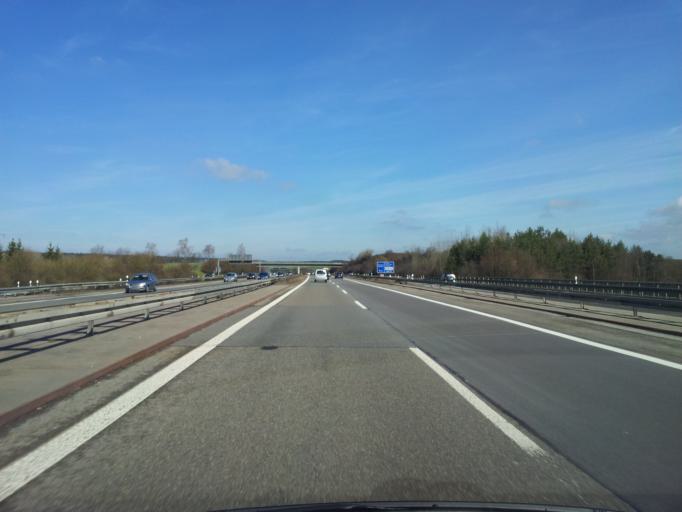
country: DE
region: Baden-Wuerttemberg
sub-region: Freiburg Region
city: Deisslingen
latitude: 48.0904
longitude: 8.5927
